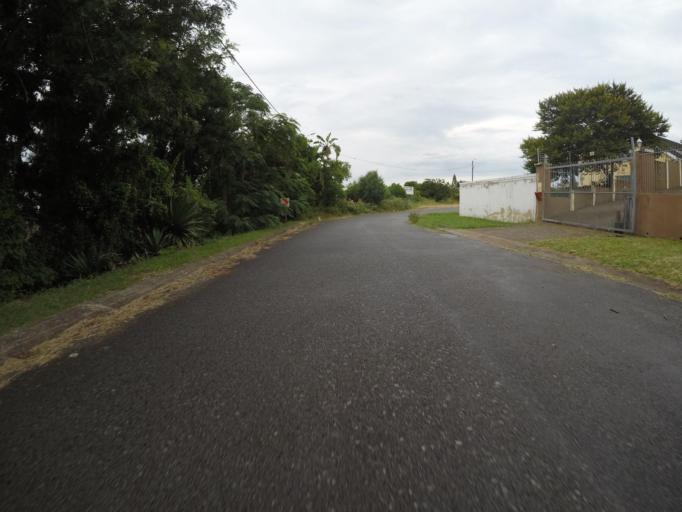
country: ZA
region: Eastern Cape
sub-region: Buffalo City Metropolitan Municipality
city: East London
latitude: -32.9638
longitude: 27.8441
